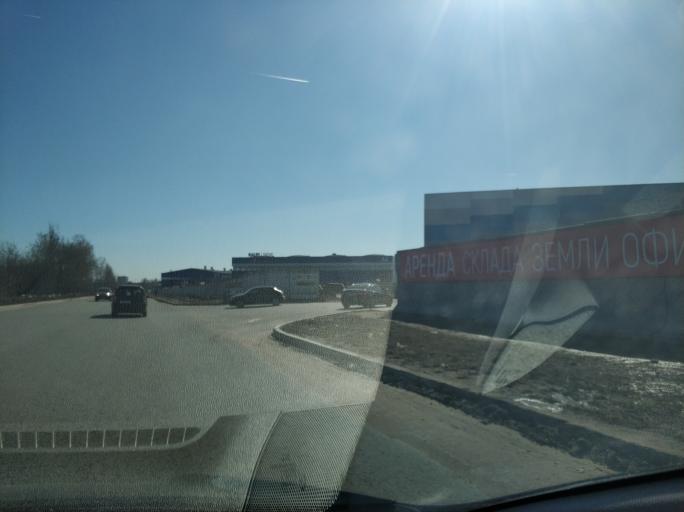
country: RU
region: Leningrad
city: Bugry
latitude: 60.0660
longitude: 30.3828
